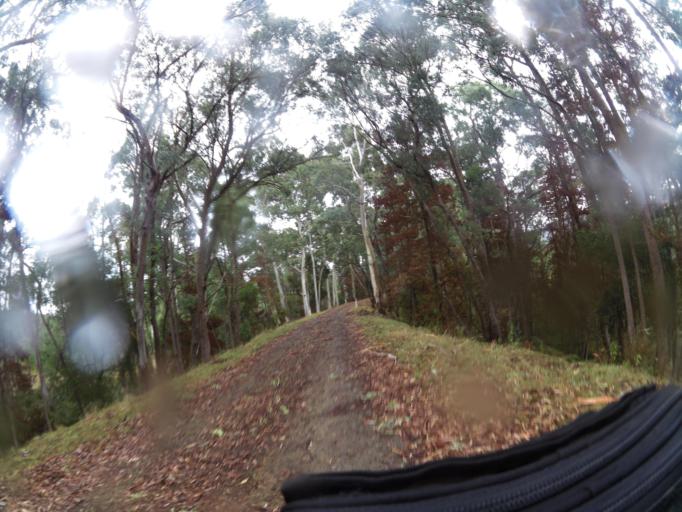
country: AU
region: New South Wales
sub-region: Greater Hume Shire
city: Holbrook
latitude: -36.2243
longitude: 147.5802
